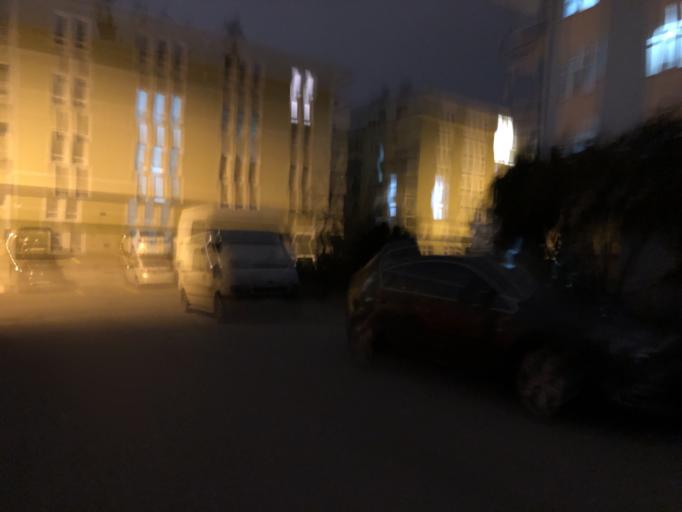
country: TR
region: Ankara
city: Ankara
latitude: 39.9807
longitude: 32.8350
